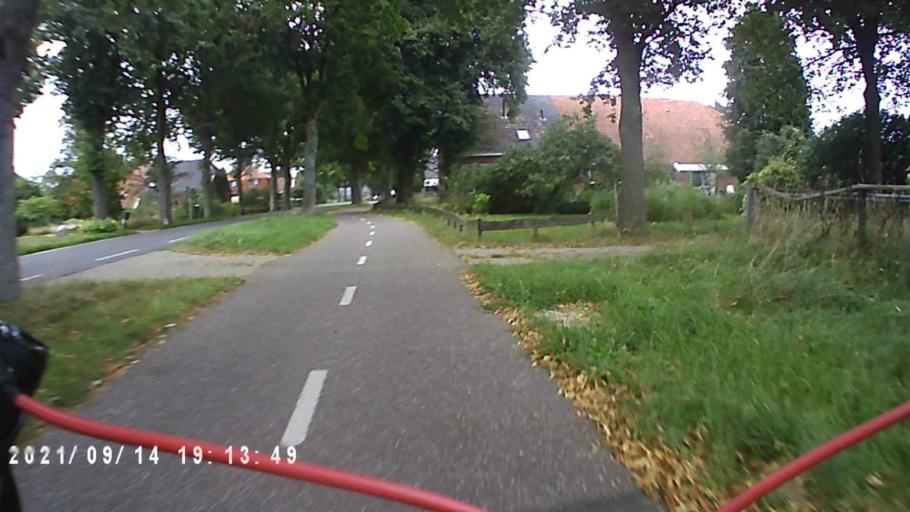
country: NL
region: Drenthe
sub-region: Gemeente Aa en Hunze
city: Anloo
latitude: 53.0671
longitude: 6.7080
